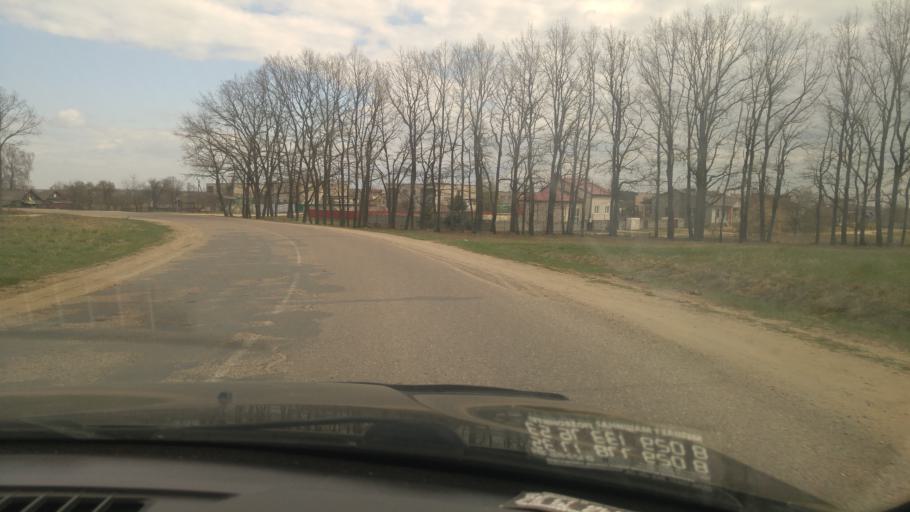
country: BY
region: Minsk
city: Rudzyensk
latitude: 53.6547
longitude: 27.8034
